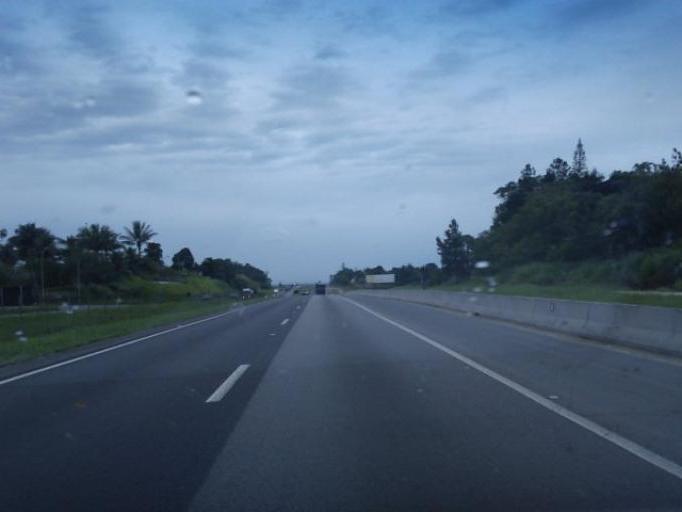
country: BR
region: Sao Paulo
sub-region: Registro
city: Registro
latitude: -24.4615
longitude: -47.8175
